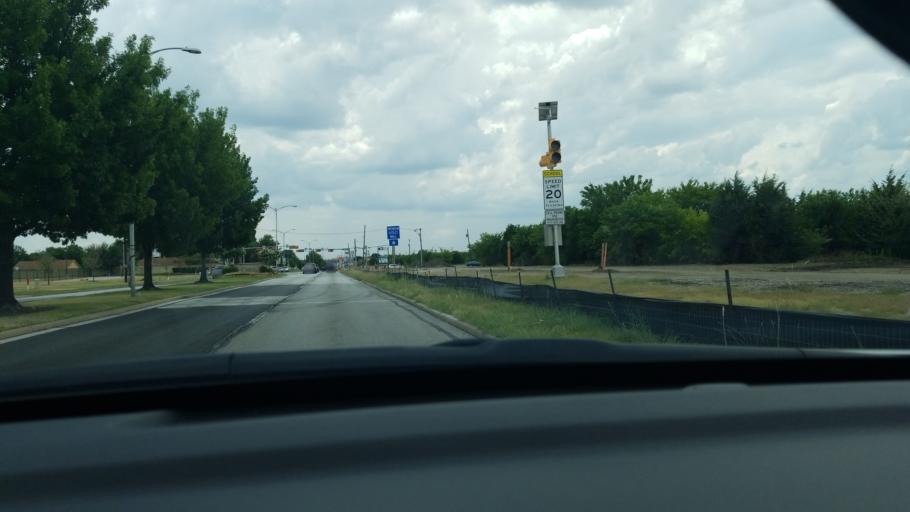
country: US
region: Texas
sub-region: Dallas County
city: Grand Prairie
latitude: 32.6857
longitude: -97.0443
